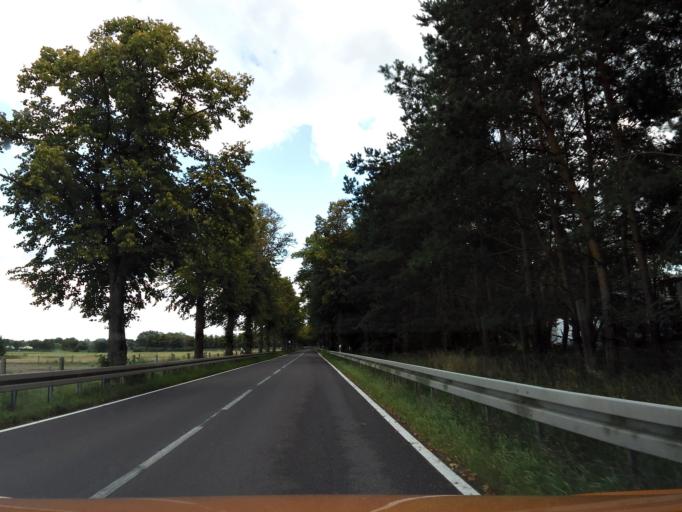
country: DE
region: Brandenburg
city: Potsdam
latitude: 52.4610
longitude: 13.0002
